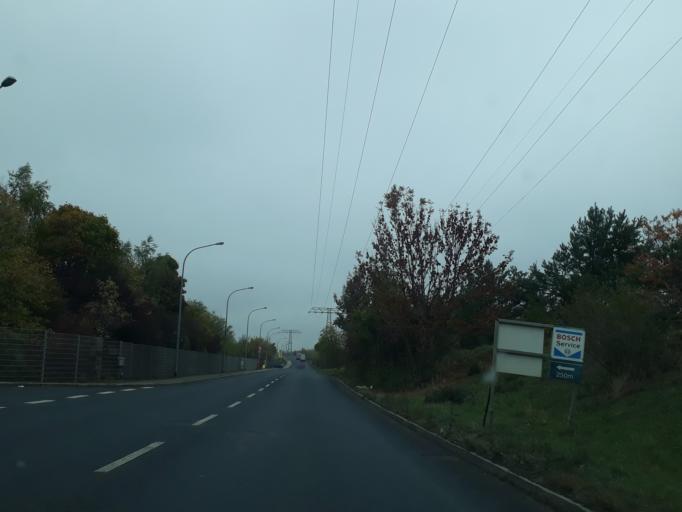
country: DE
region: Saxony
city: Radeburg
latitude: 51.2036
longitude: 13.7377
